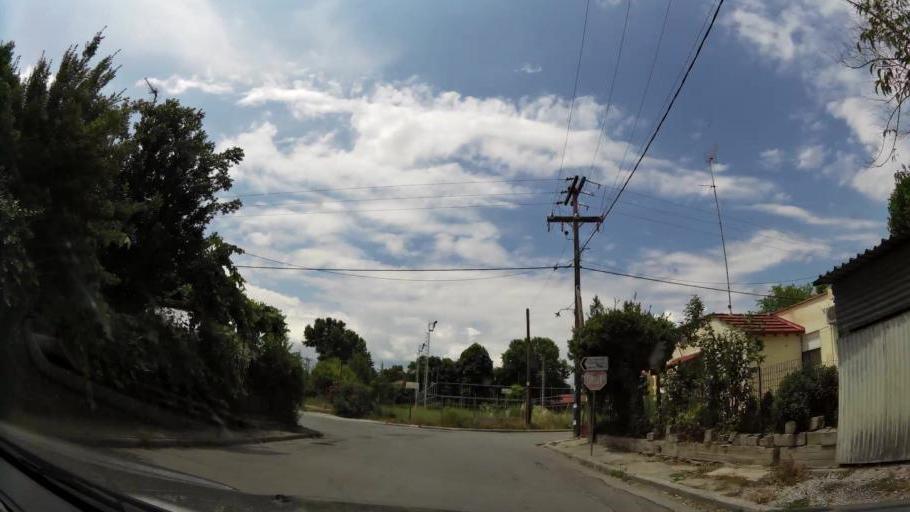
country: GR
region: Central Macedonia
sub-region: Nomos Pierias
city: Katerini
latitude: 40.2642
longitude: 22.5131
